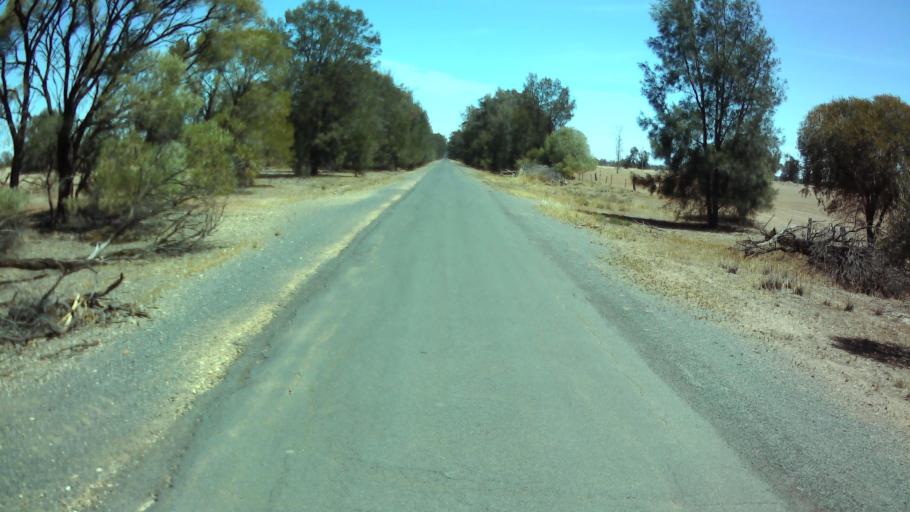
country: AU
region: New South Wales
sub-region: Weddin
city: Grenfell
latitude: -33.8756
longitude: 147.6910
